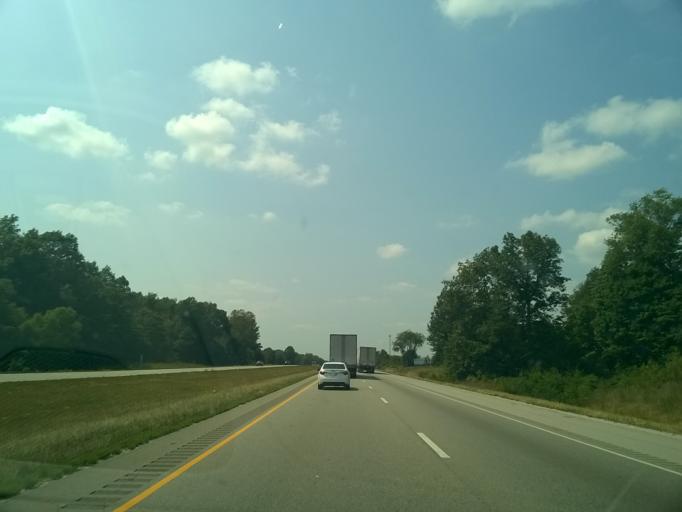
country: US
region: Indiana
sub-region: Vigo County
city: Seelyville
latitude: 39.4459
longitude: -87.2308
